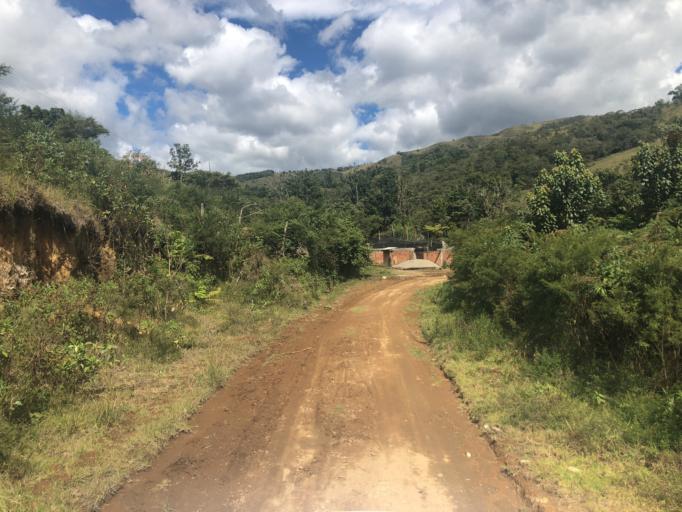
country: CO
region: Cauca
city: Silvia
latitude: 2.6823
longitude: -76.4360
